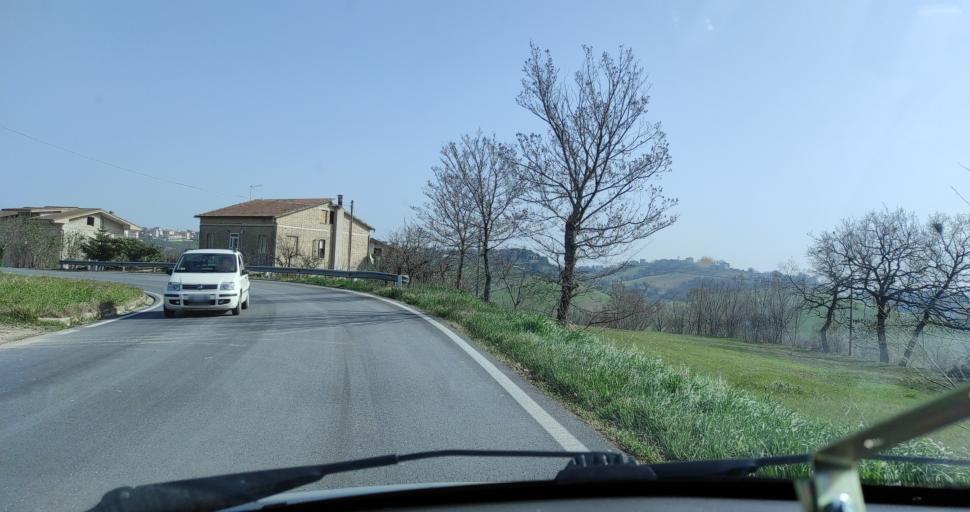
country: IT
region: The Marches
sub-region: Provincia di Macerata
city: Mogliano
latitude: 43.1784
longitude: 13.4543
